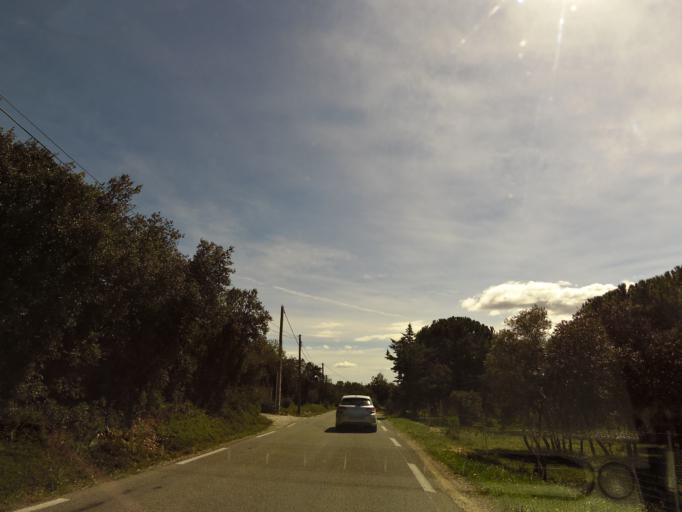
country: FR
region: Languedoc-Roussillon
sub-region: Departement du Gard
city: Langlade
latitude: 43.7865
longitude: 4.2674
